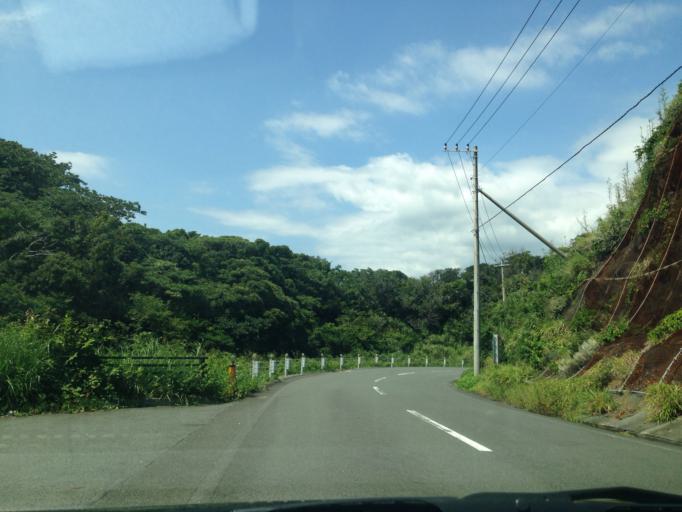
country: JP
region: Shizuoka
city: Shimoda
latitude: 34.6137
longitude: 138.8272
